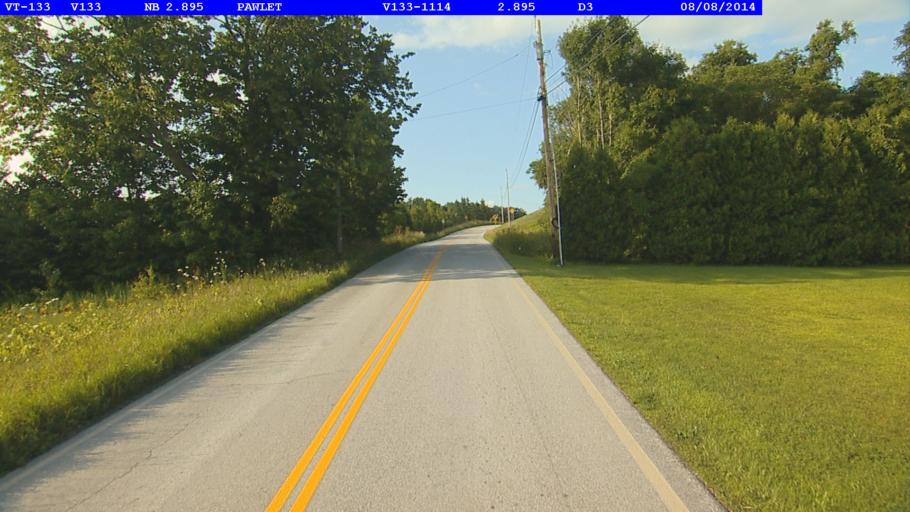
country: US
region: New York
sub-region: Washington County
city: Granville
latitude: 43.3732
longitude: -73.1451
